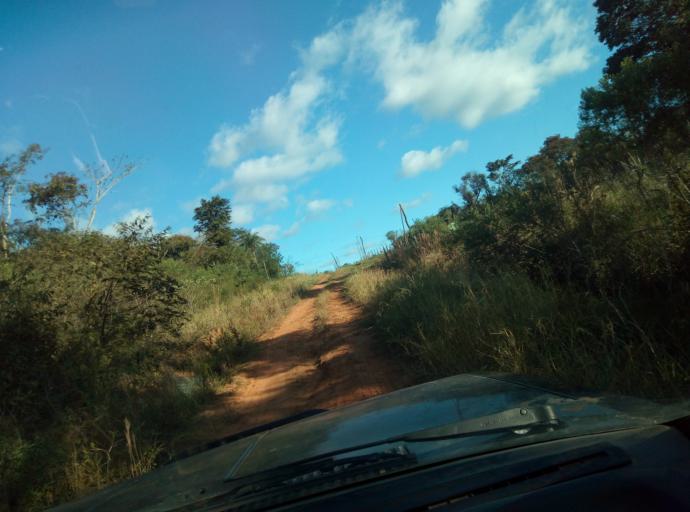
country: PY
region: Caaguazu
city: Carayao
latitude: -25.1729
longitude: -56.2734
